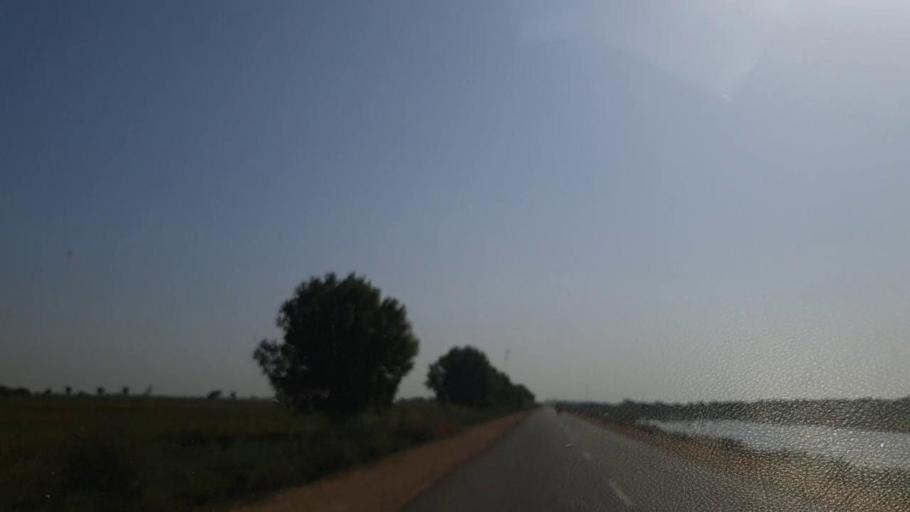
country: PK
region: Sindh
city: Jati
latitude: 24.5341
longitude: 68.2786
